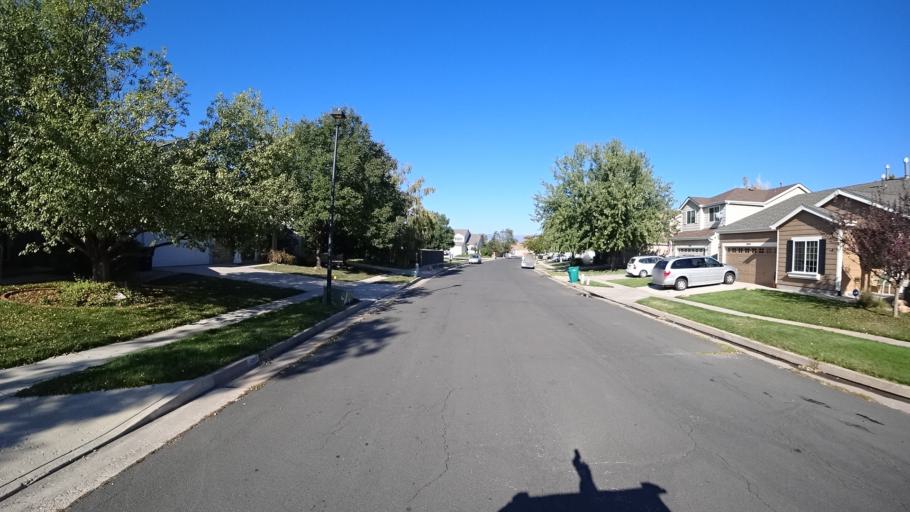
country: US
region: Colorado
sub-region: El Paso County
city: Cimarron Hills
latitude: 38.8814
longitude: -104.6946
